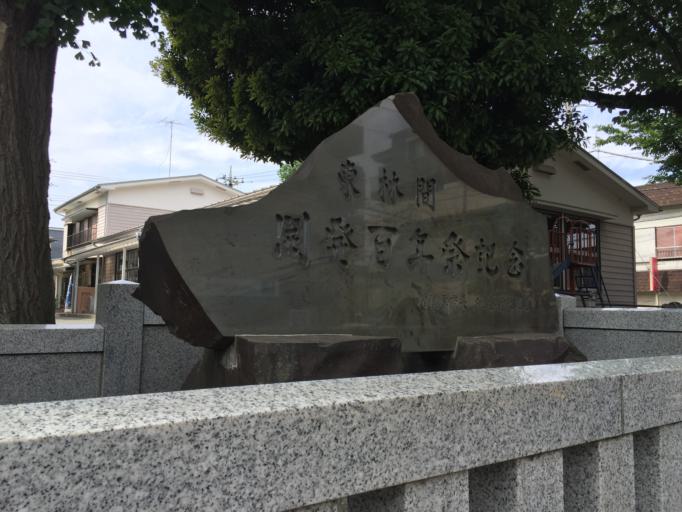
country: JP
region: Tokyo
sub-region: Machida-shi
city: Machida
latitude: 35.5197
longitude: 139.4354
